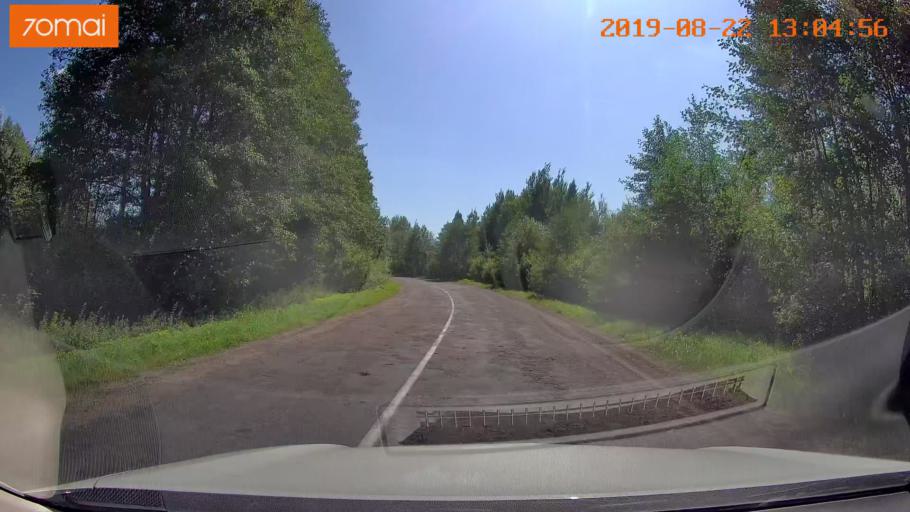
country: BY
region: Minsk
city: Prawdzinski
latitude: 53.3641
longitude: 27.8290
